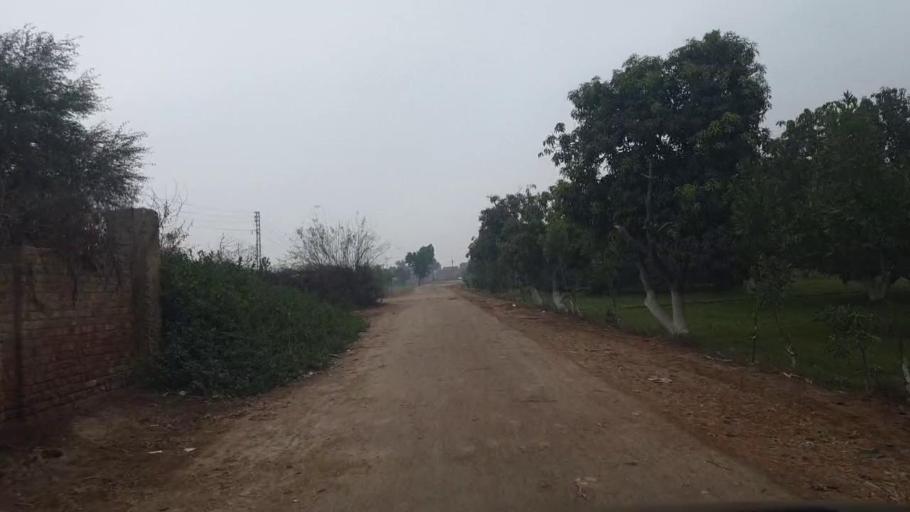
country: PK
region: Sindh
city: Tando Adam
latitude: 25.8039
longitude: 68.6674
